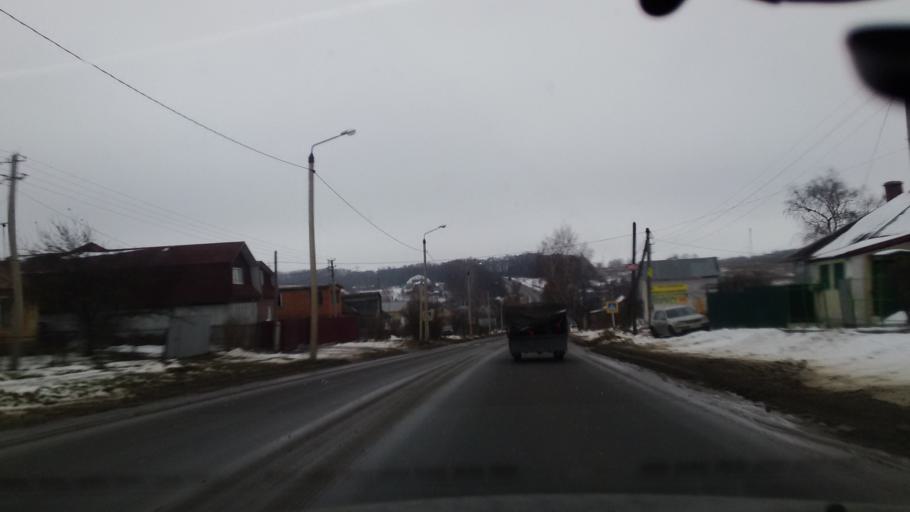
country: RU
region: Tula
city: Skuratovskiy
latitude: 54.1342
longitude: 37.6785
